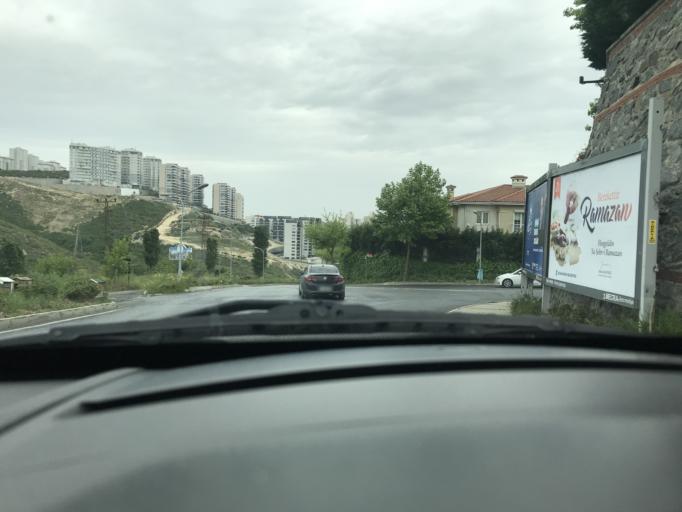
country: TR
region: Istanbul
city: Esenyurt
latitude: 41.0891
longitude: 28.6823
